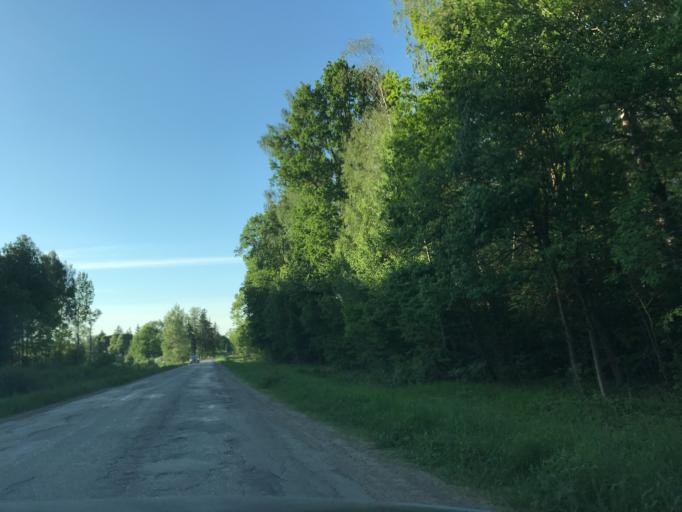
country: LV
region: Ozolnieku
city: Ozolnieki
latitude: 56.6061
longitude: 23.7905
